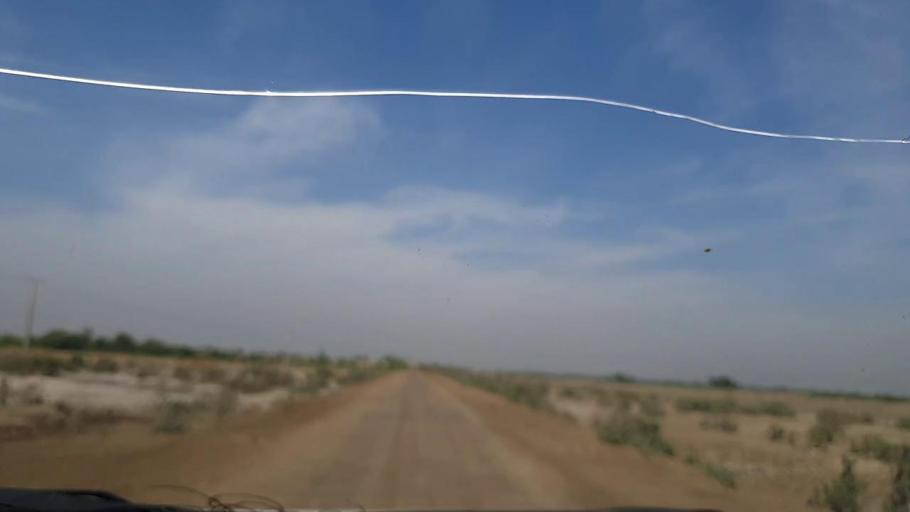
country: PK
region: Sindh
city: Pithoro
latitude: 25.4915
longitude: 69.4564
